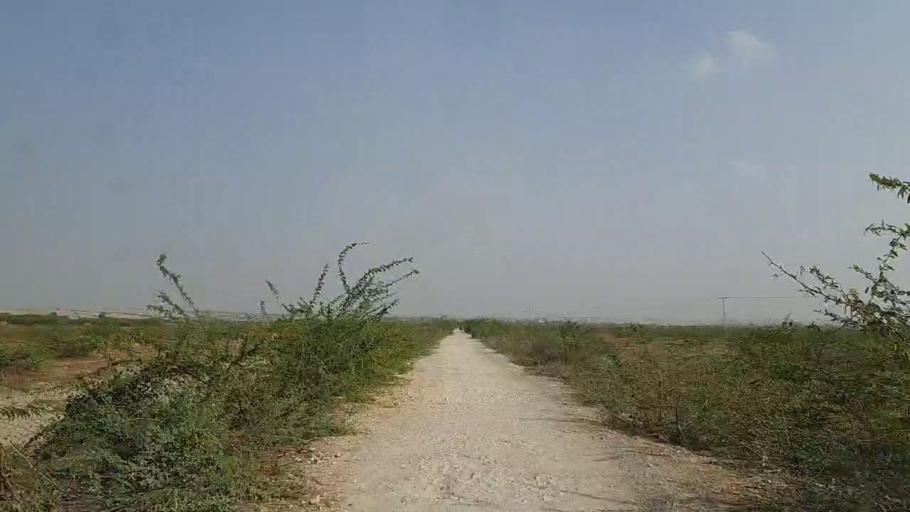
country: PK
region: Sindh
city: Naukot
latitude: 24.6664
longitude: 69.2766
